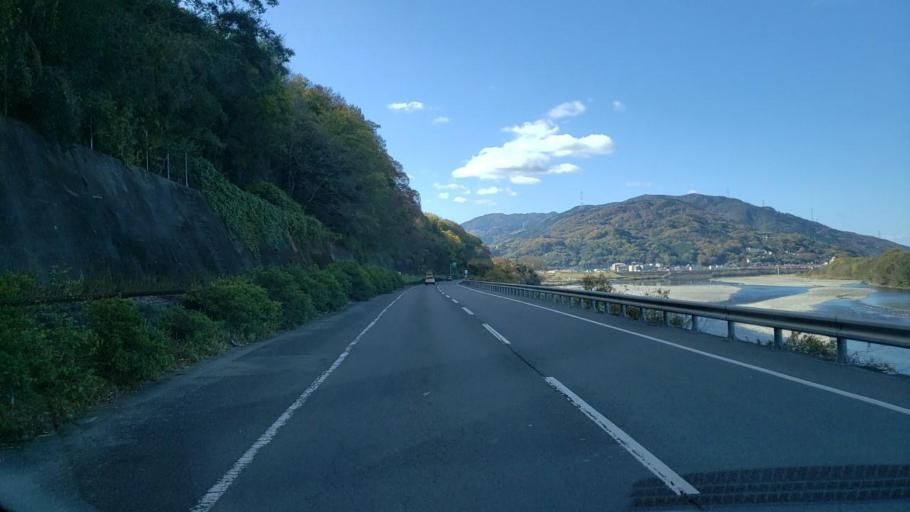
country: JP
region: Tokushima
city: Wakimachi
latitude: 34.0608
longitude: 134.1868
